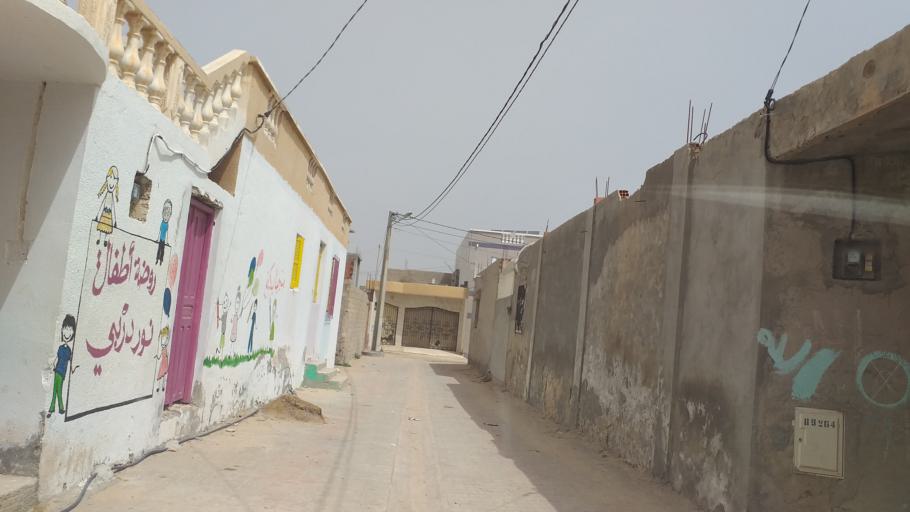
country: TN
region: Qabis
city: Gabes
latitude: 33.9433
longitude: 10.0622
